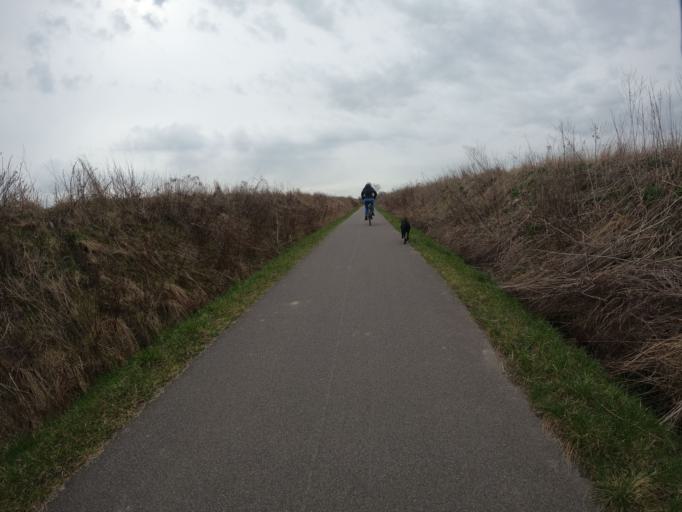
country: PL
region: West Pomeranian Voivodeship
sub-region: Powiat gryficki
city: Trzebiatow
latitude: 54.0984
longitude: 15.2809
